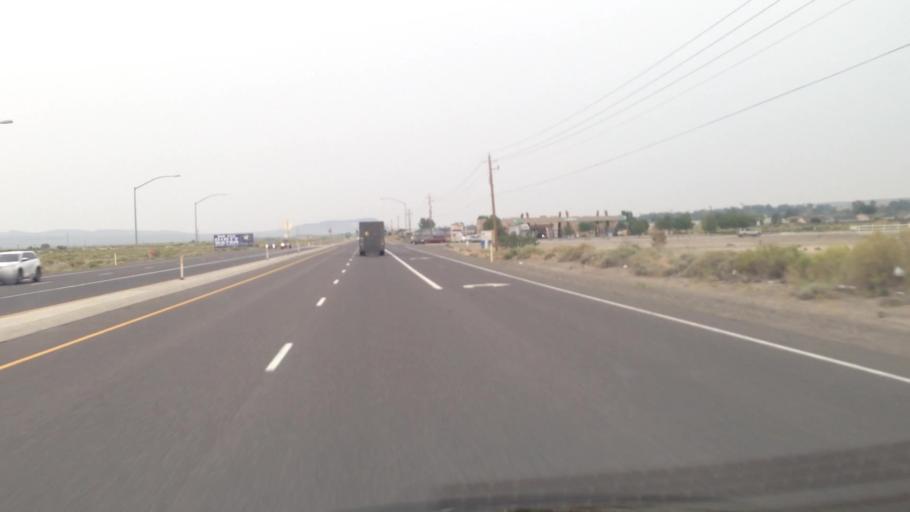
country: US
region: Nevada
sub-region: Lyon County
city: Fernley
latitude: 39.5986
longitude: -119.1997
